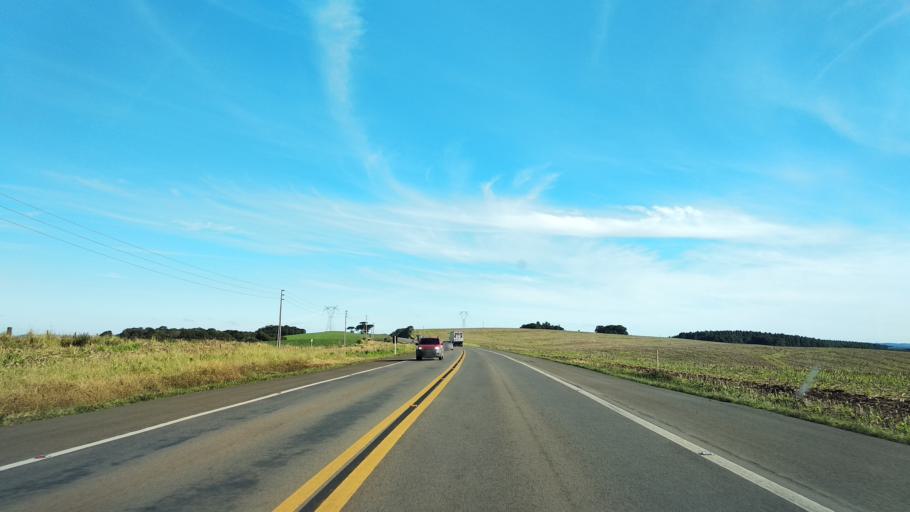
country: BR
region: Santa Catarina
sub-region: Celso Ramos
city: Celso Ramos
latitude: -27.4988
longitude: -51.3409
